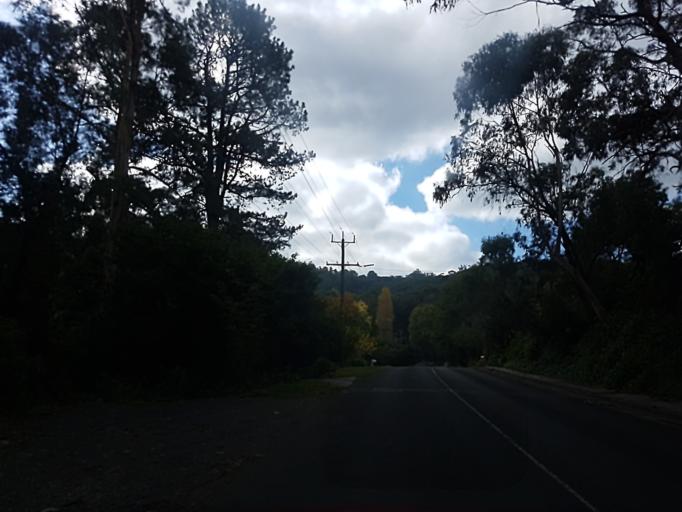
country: AU
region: Victoria
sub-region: Yarra Ranges
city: Tremont
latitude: -37.8973
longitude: 145.3340
